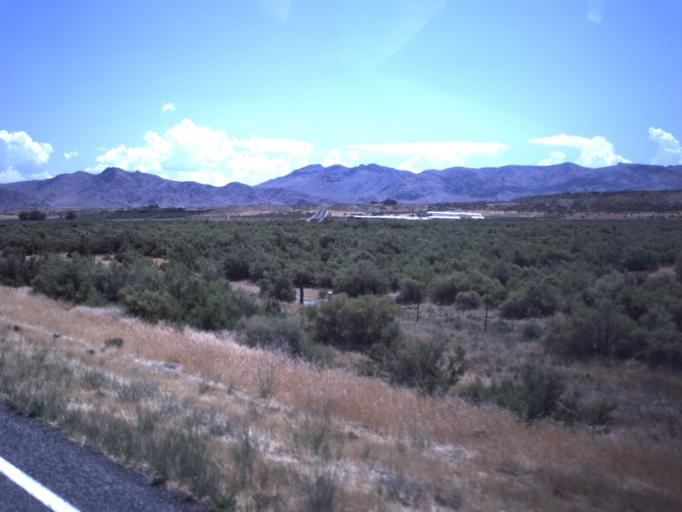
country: US
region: Utah
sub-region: Millard County
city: Delta
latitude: 39.5279
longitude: -112.3507
